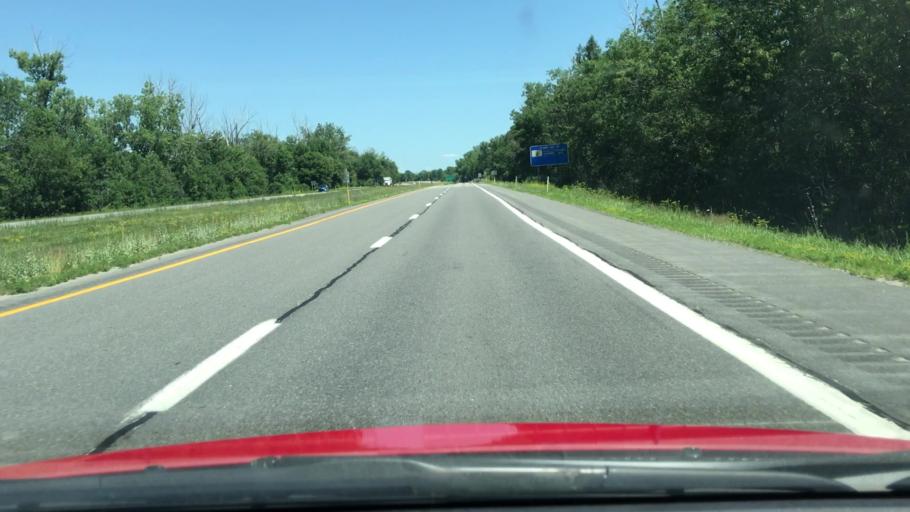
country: US
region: New York
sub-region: Clinton County
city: Plattsburgh
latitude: 44.7197
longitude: -73.4535
